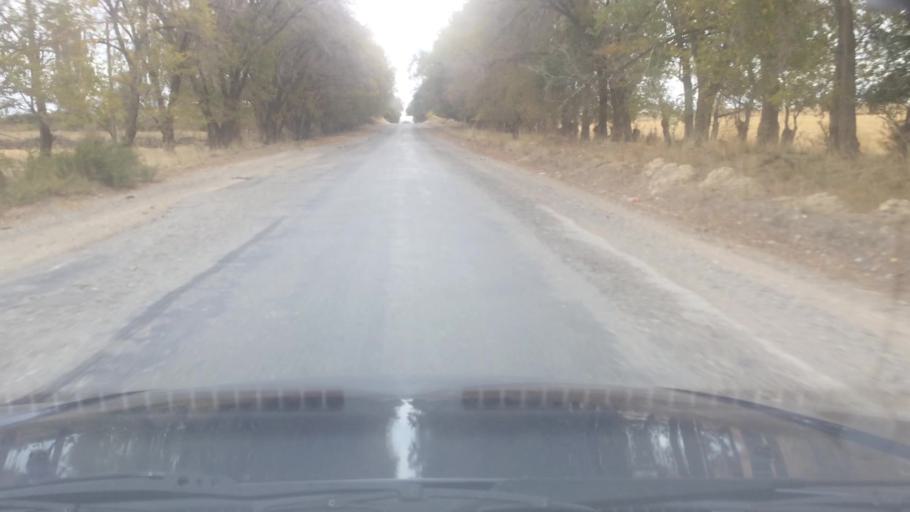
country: KG
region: Ysyk-Koel
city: Balykchy
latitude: 42.3034
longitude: 76.4783
